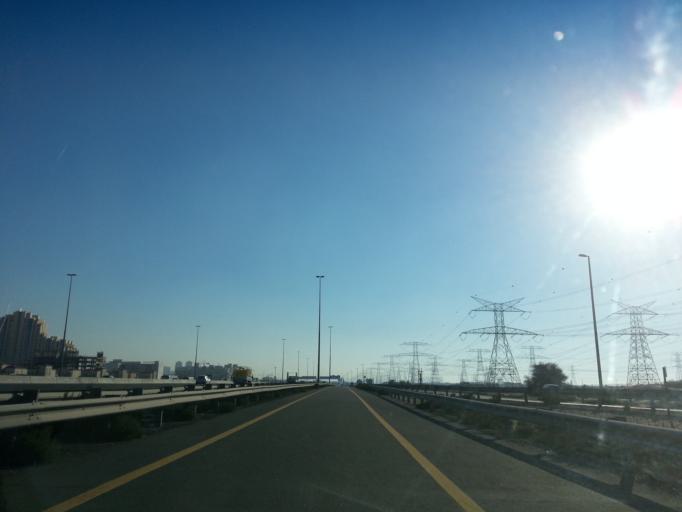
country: AE
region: Dubai
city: Dubai
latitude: 25.0753
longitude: 55.2087
